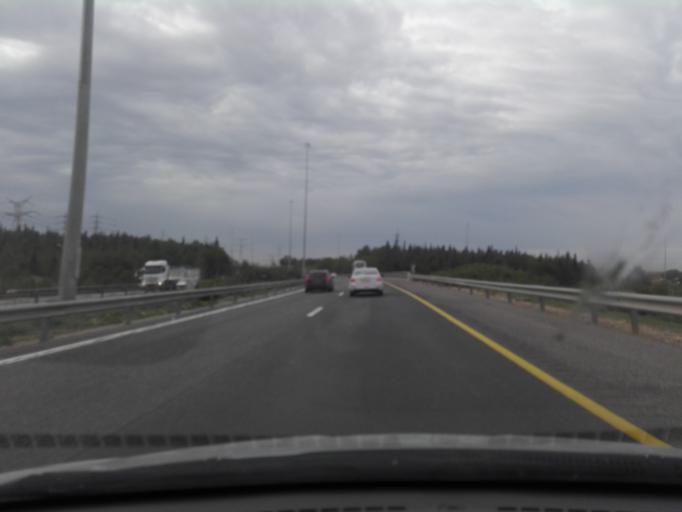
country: IL
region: Central District
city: Lod
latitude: 31.9609
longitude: 34.9402
